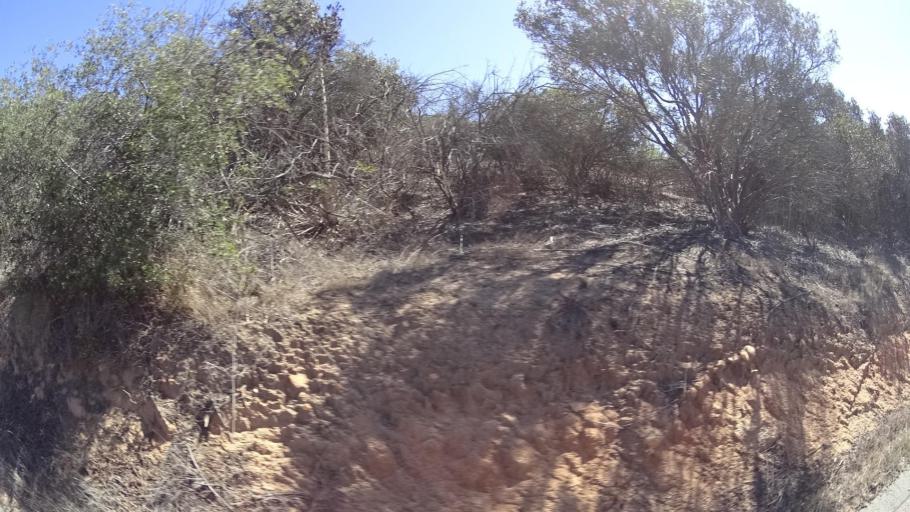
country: US
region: California
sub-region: San Diego County
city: Harbison Canyon
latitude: 32.7928
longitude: -116.8039
